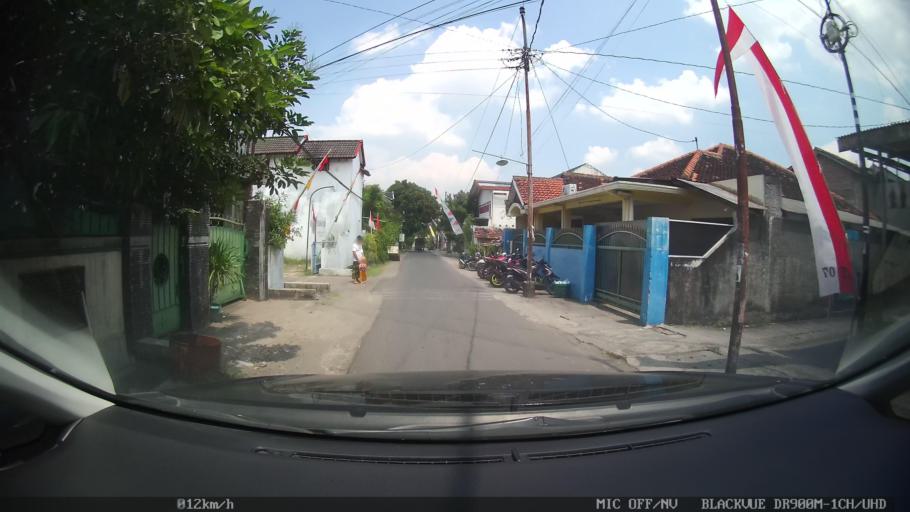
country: ID
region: Daerah Istimewa Yogyakarta
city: Yogyakarta
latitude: -7.8180
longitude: 110.4041
